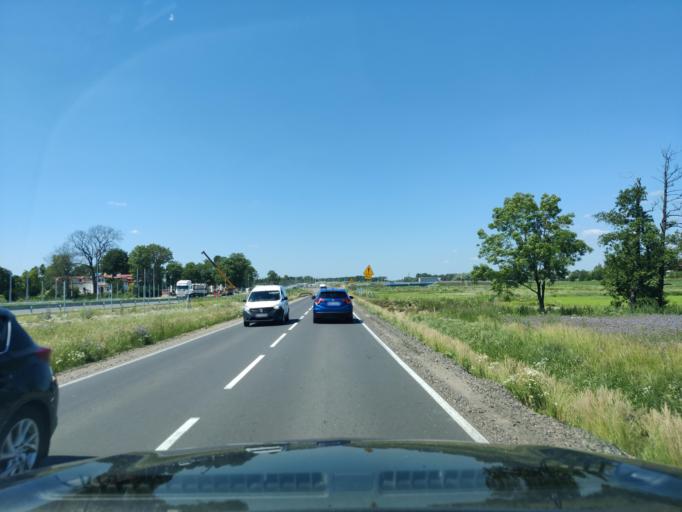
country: PL
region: Masovian Voivodeship
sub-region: Powiat plonski
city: Baboszewo
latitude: 52.7022
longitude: 20.3388
